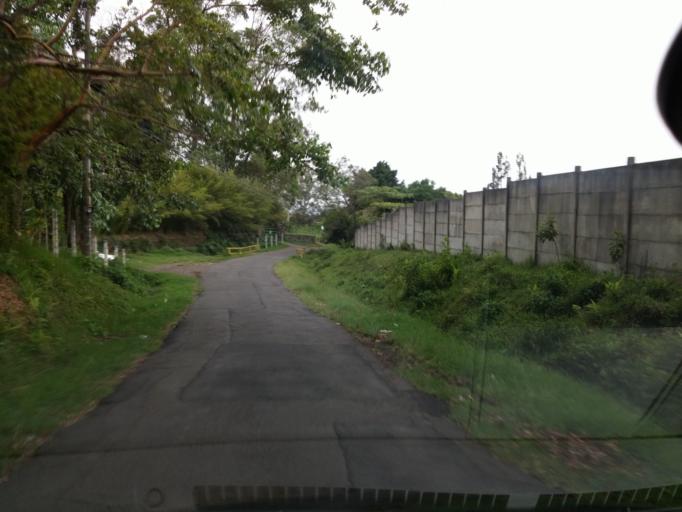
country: CR
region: Heredia
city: San Josecito
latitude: 10.0358
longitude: -84.0977
